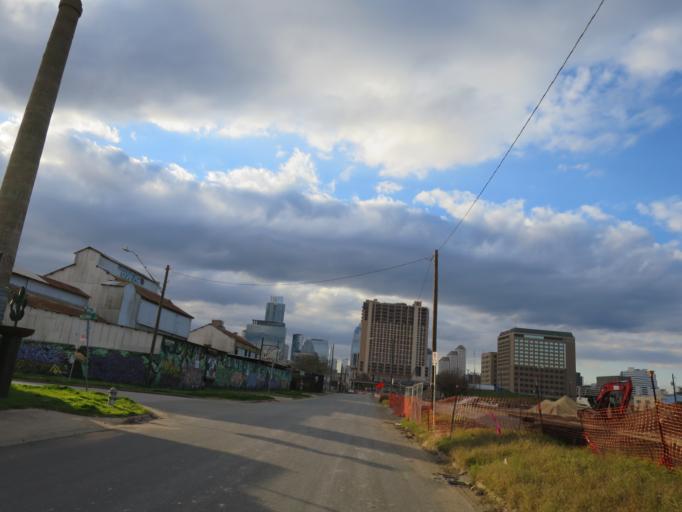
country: US
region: Texas
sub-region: Travis County
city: Austin
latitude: 30.2629
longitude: -97.7321
